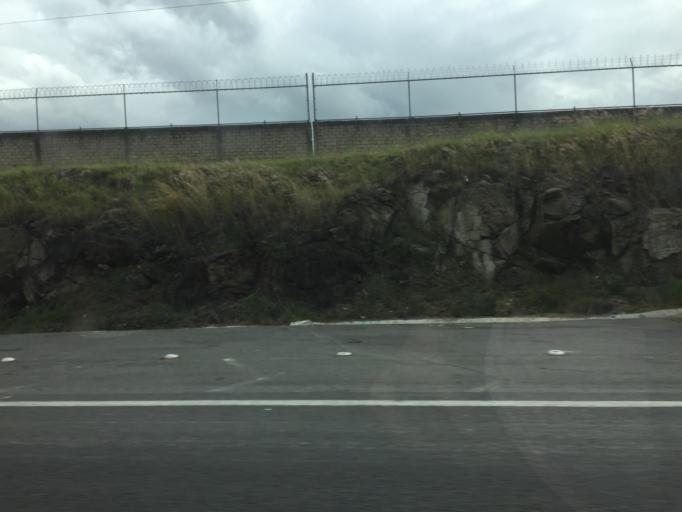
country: MX
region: Jalisco
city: Puente Grande
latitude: 20.6037
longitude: -103.1265
